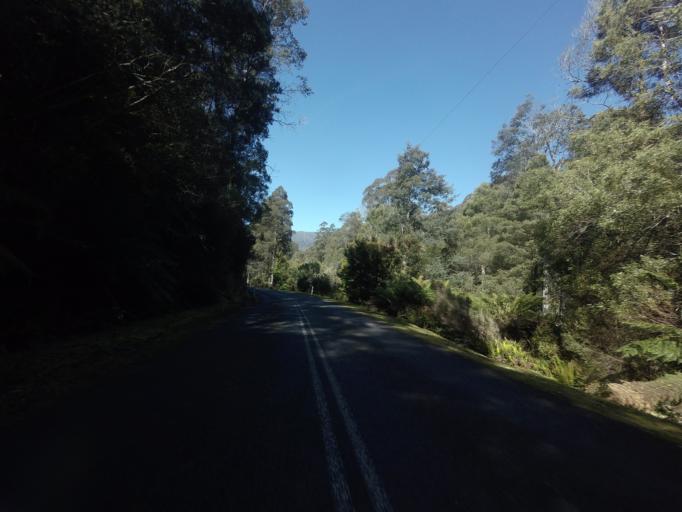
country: AU
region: Tasmania
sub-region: Derwent Valley
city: New Norfolk
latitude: -42.7682
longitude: 146.5641
